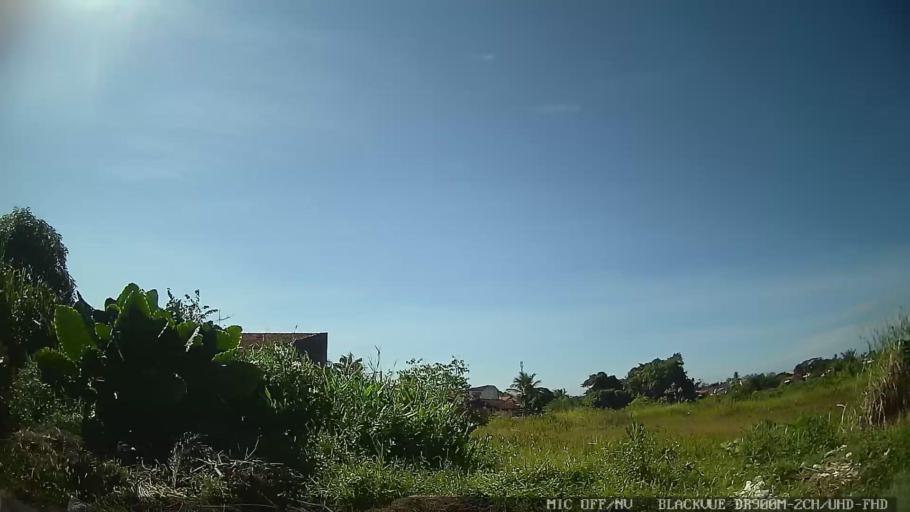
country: BR
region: Sao Paulo
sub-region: Itanhaem
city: Itanhaem
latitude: -24.2136
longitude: -46.8607
